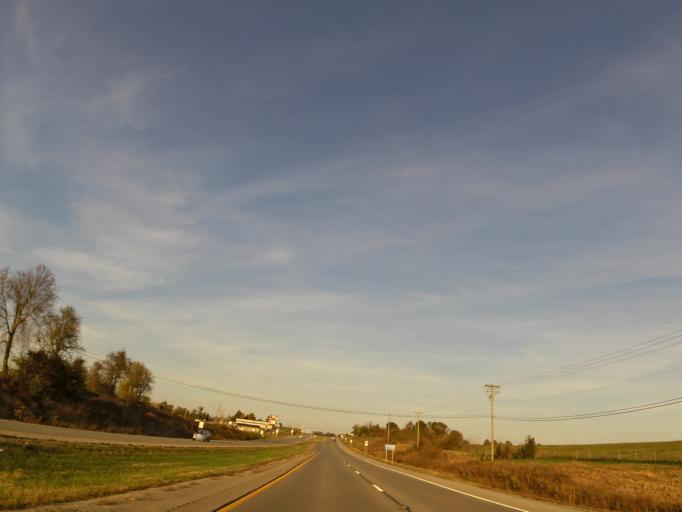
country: US
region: Kentucky
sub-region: Garrard County
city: Lancaster
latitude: 37.7045
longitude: -84.6585
